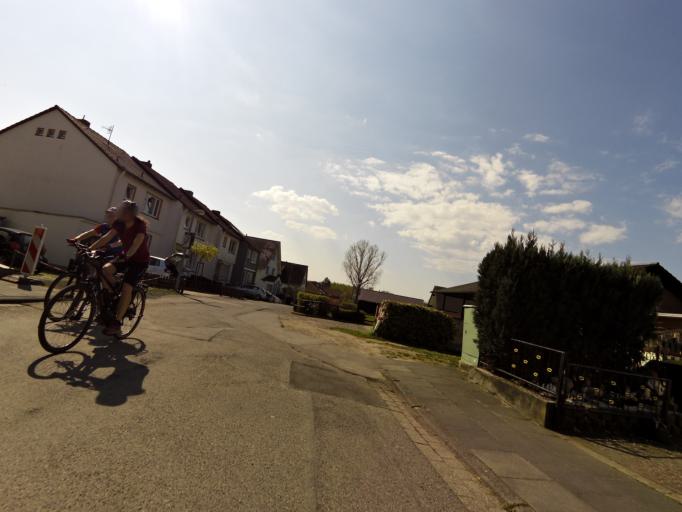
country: DE
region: North Rhine-Westphalia
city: Meckenheim
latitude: 50.6761
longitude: 7.0225
